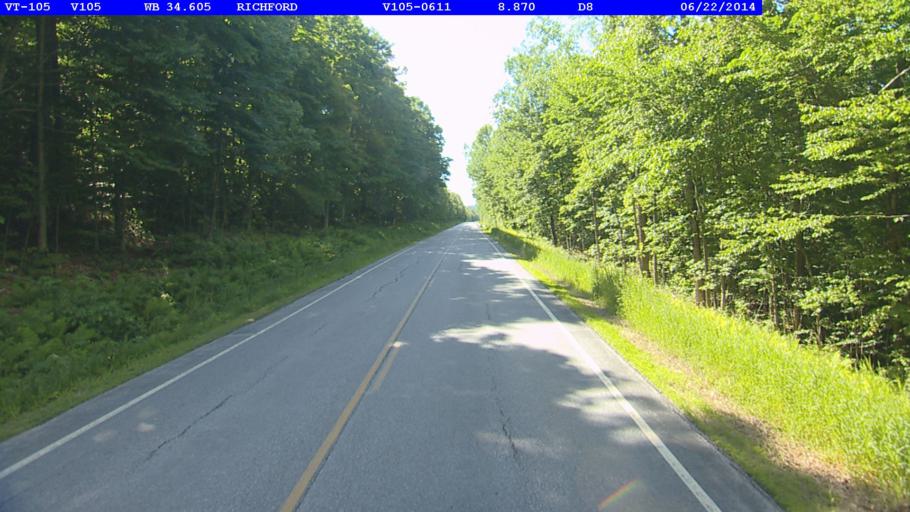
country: US
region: Vermont
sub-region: Franklin County
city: Richford
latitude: 44.9884
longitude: -72.5557
